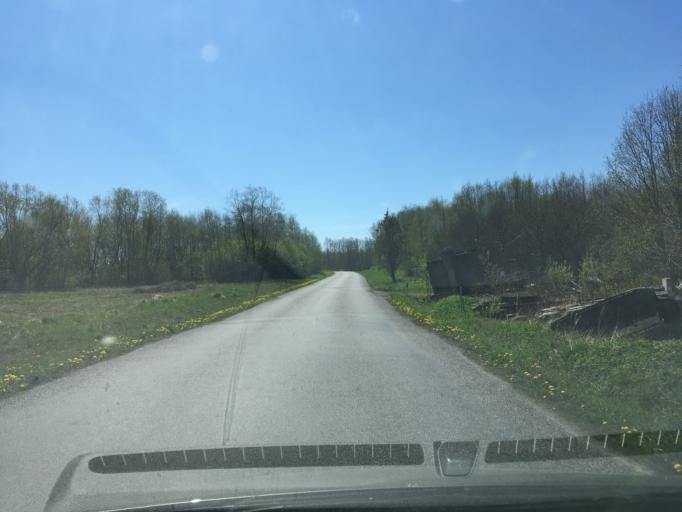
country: EE
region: Harju
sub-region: Raasiku vald
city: Arukula
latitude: 59.4056
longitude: 25.0780
